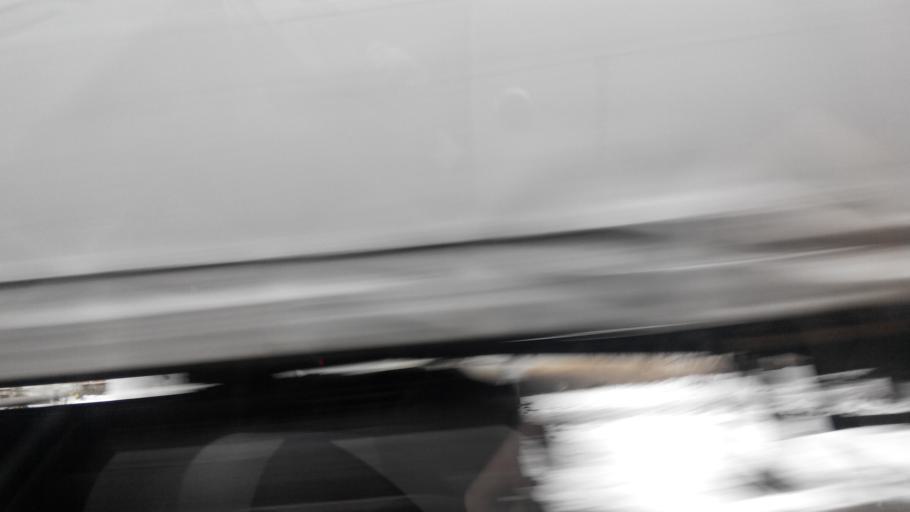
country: RU
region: Tula
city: Uzlovaya
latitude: 53.9653
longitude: 38.1650
